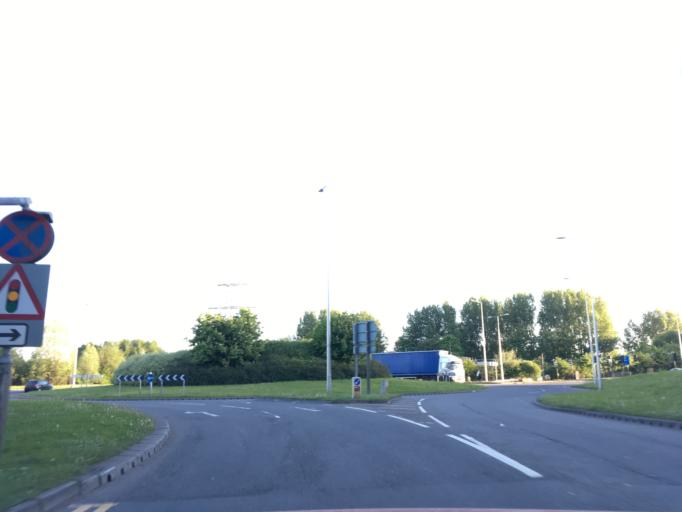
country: GB
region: Wales
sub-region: Newport
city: Newport
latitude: 51.5683
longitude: -3.0035
